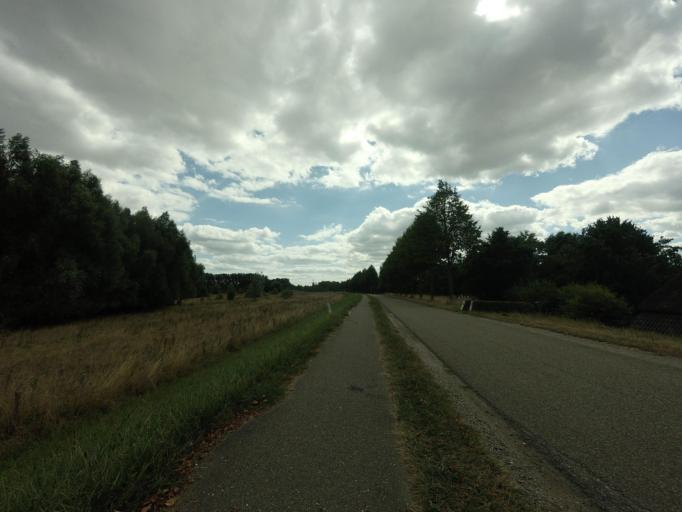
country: NL
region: Gelderland
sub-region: Gemeente Wijchen
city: Bergharen
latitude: 51.8039
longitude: 5.6472
